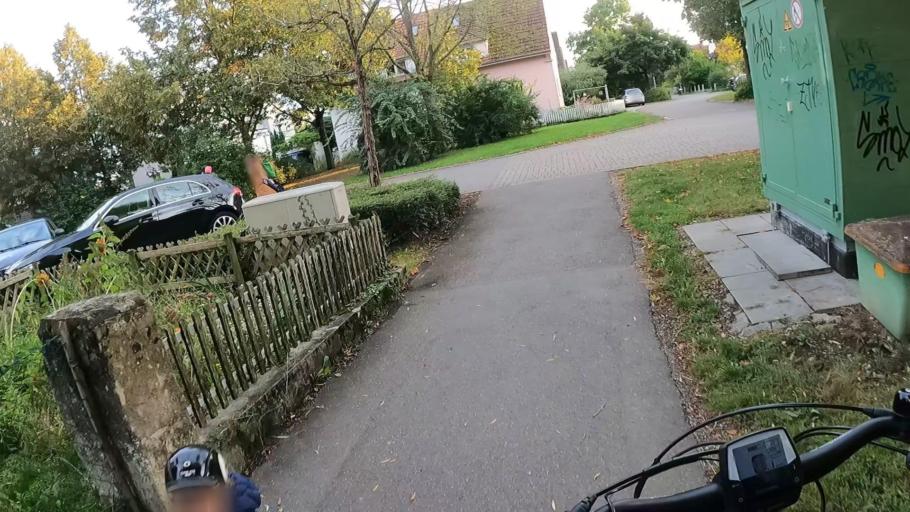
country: DE
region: Baden-Wuerttemberg
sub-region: Freiburg Region
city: Radolfzell am Bodensee
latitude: 47.7423
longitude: 8.9614
